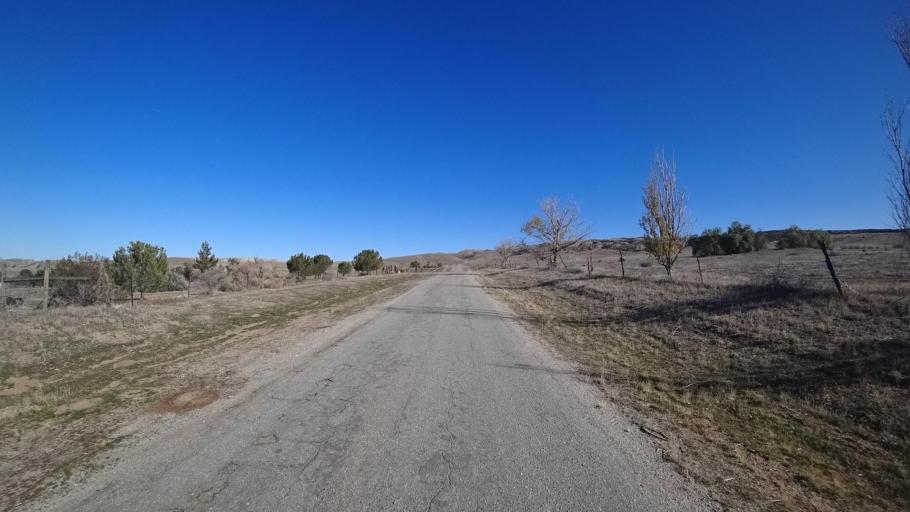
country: US
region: California
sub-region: Kern County
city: Maricopa
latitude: 34.9382
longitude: -119.4620
